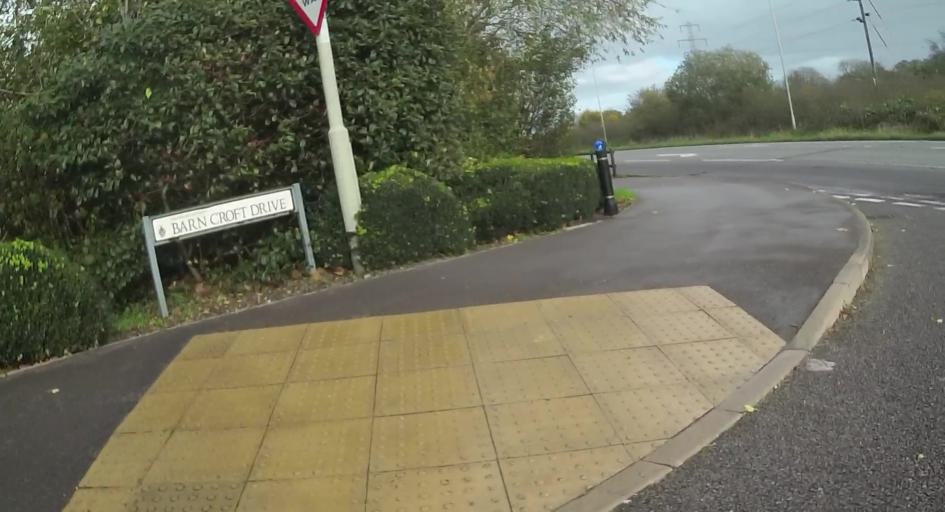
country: GB
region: England
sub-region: Wokingham
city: Lower Earley
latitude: 51.4244
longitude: -0.9069
